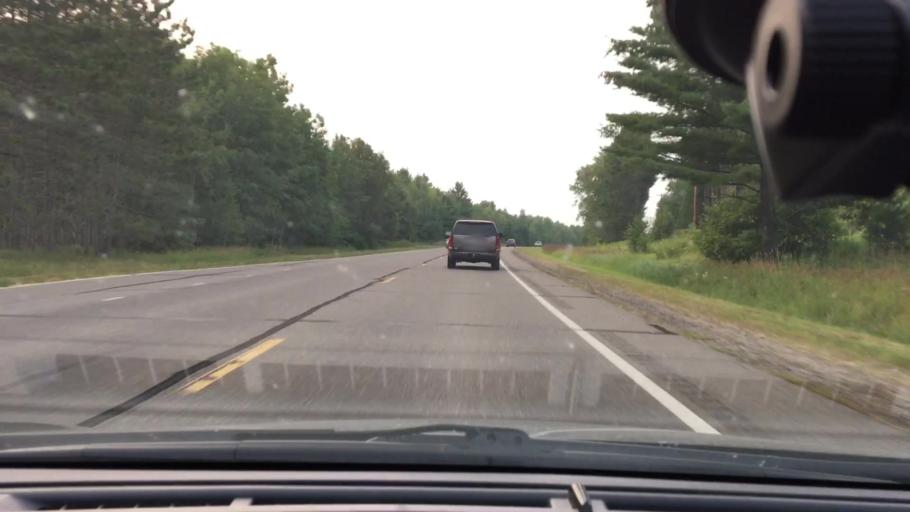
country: US
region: Minnesota
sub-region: Crow Wing County
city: Crosby
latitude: 46.4605
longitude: -93.8850
